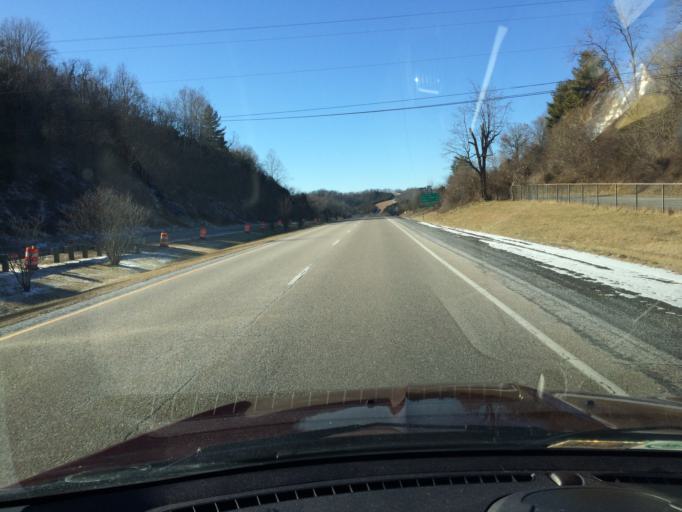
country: US
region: Virginia
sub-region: Rockbridge County
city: East Lexington
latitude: 37.7578
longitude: -79.4126
